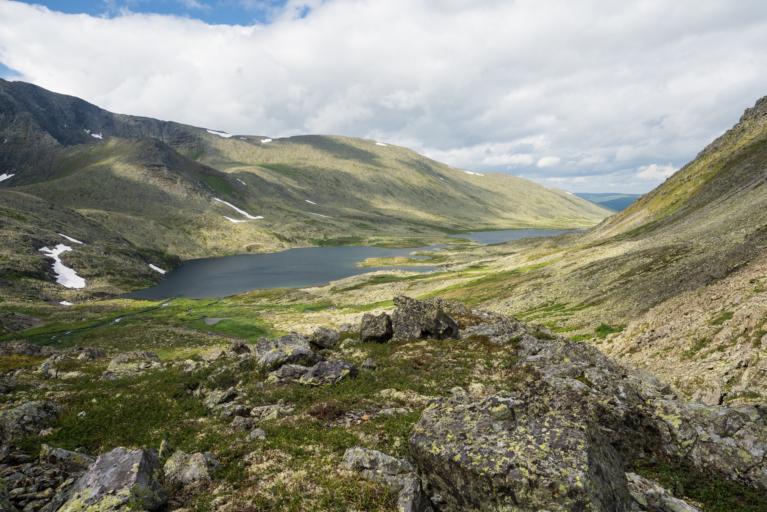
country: RU
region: Komi Republic
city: Synya
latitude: 64.8260
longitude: 59.2622
